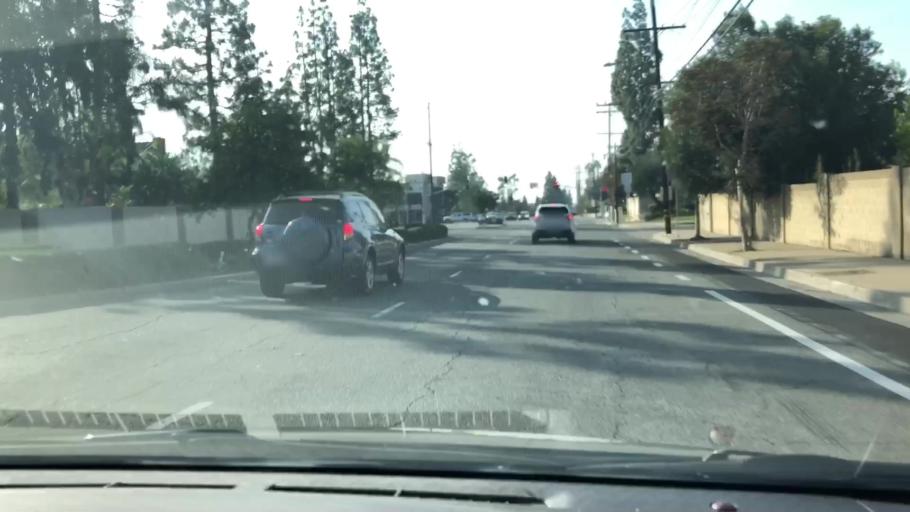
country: US
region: California
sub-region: Orange County
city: Villa Park
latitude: 33.8105
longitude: -117.8204
